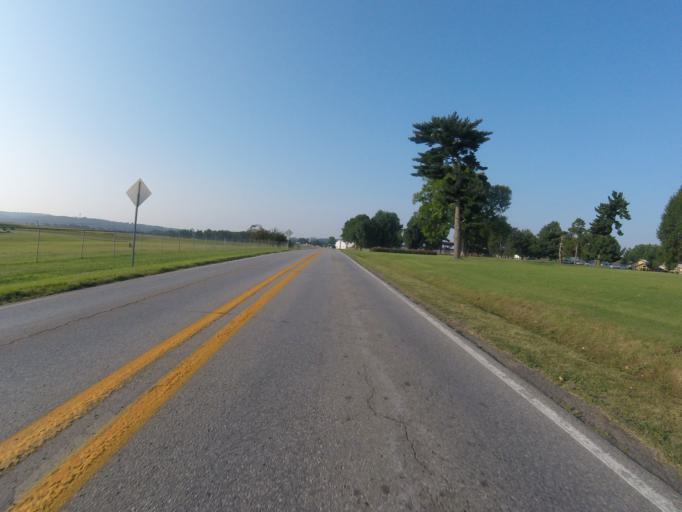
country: US
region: Arkansas
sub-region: Washington County
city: Johnson
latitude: 36.1000
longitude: -94.1774
